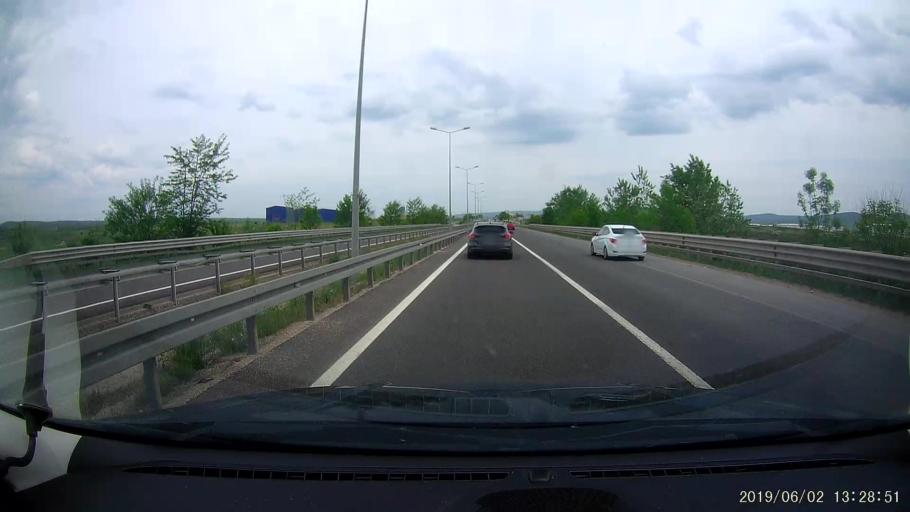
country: TR
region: Cankiri
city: Cerkes
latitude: 40.8140
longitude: 32.9171
